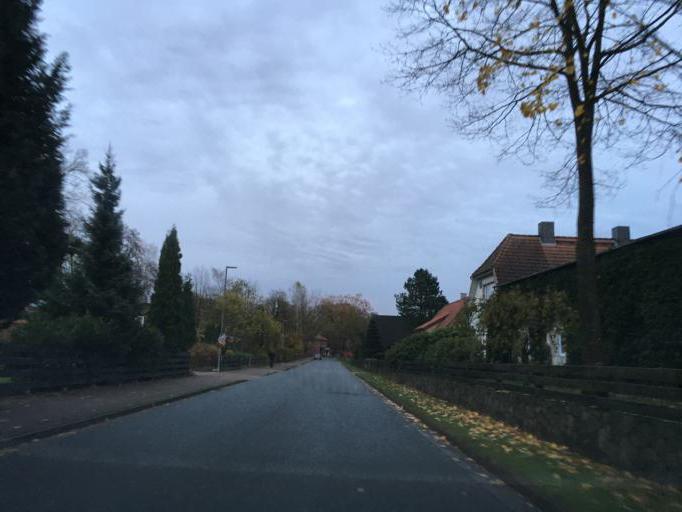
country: DE
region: Lower Saxony
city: Bispingen
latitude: 53.0964
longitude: 10.0225
